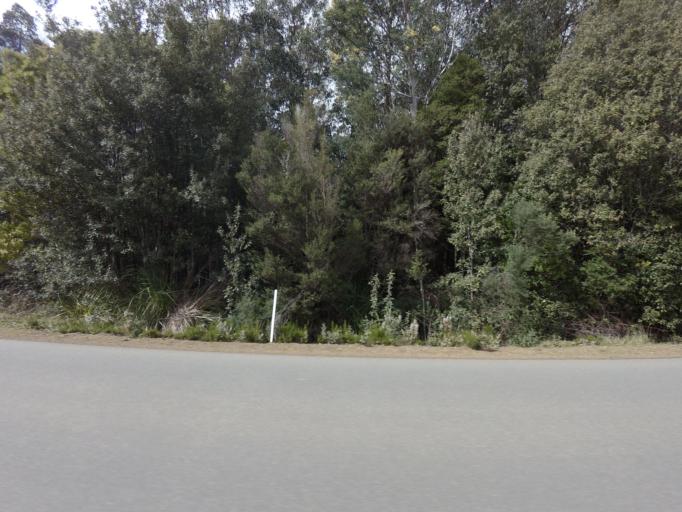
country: AU
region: Tasmania
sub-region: Huon Valley
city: Geeveston
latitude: -43.3612
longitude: 146.9584
